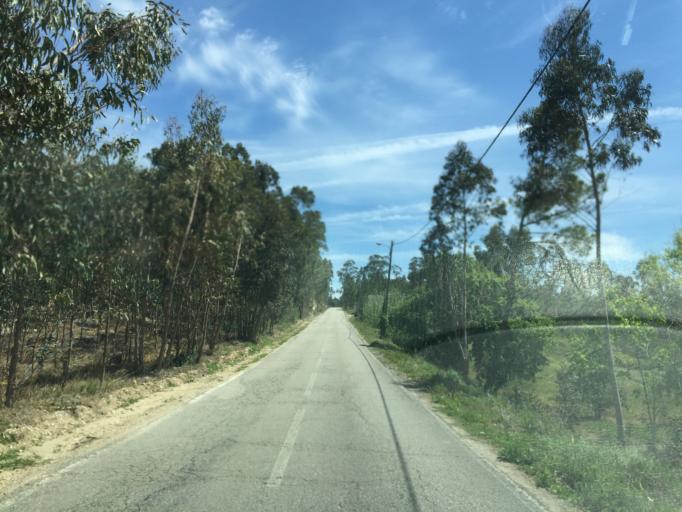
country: PT
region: Leiria
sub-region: Pombal
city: Lourical
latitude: 40.0661
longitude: -8.7248
